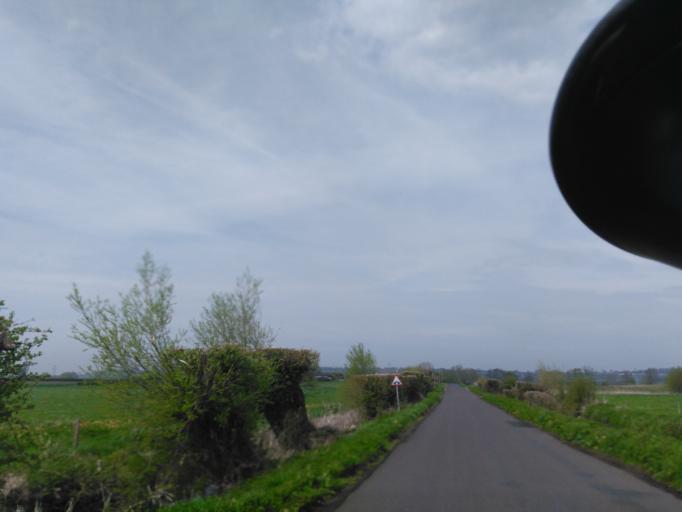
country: GB
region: England
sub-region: Somerset
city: Langport
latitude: 51.1068
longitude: -2.8192
